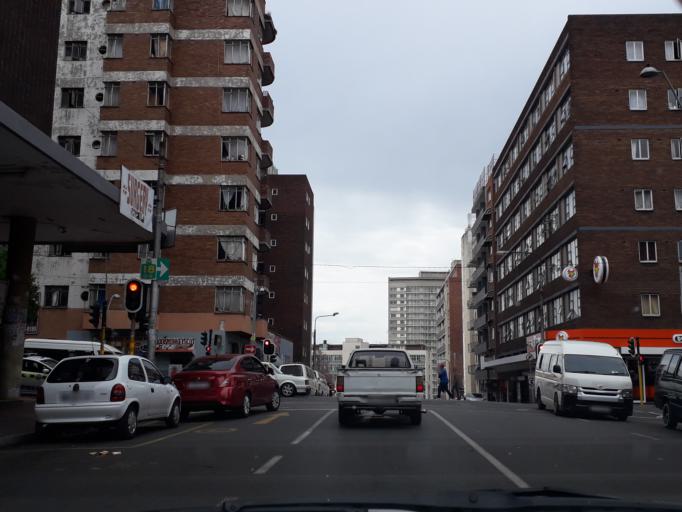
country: ZA
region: Gauteng
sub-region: City of Johannesburg Metropolitan Municipality
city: Johannesburg
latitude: -26.1896
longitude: 28.0454
